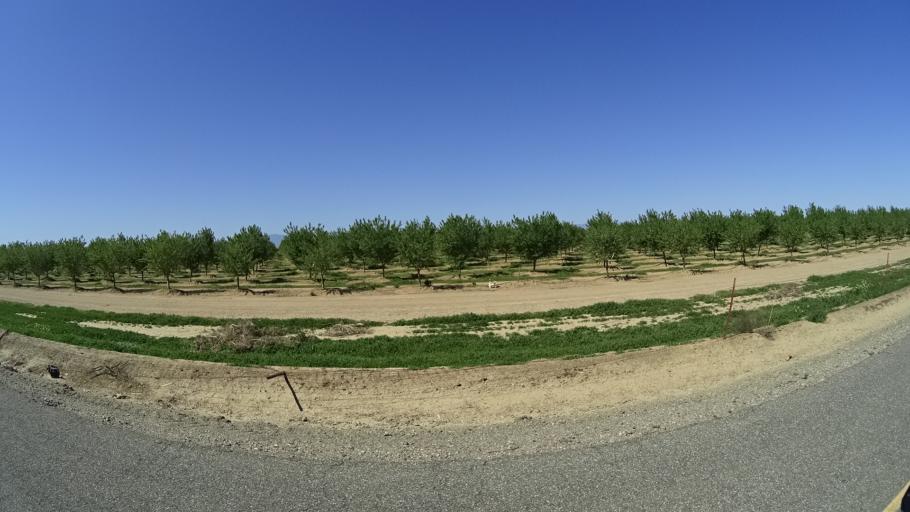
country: US
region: California
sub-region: Glenn County
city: Orland
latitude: 39.6548
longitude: -122.2532
